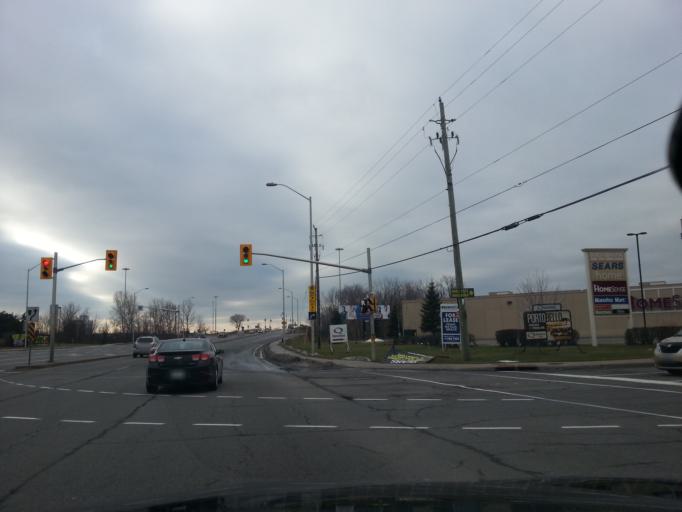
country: CA
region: Ontario
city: Ottawa
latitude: 45.4157
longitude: -75.6046
